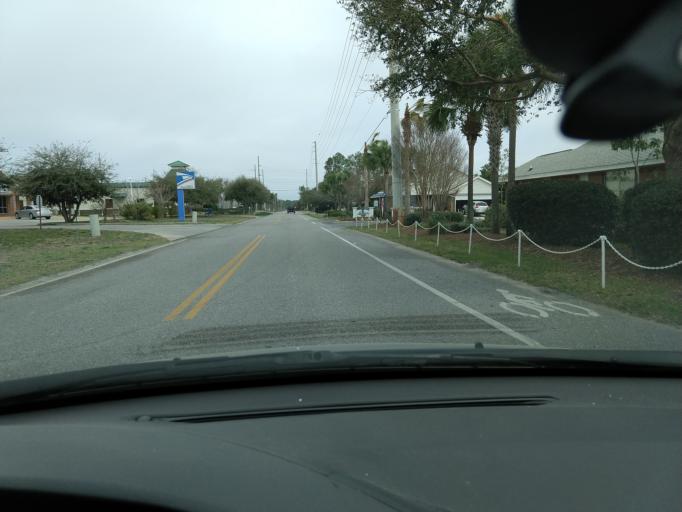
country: US
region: Florida
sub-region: Walton County
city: Miramar Beach
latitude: 30.3767
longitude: -86.3586
